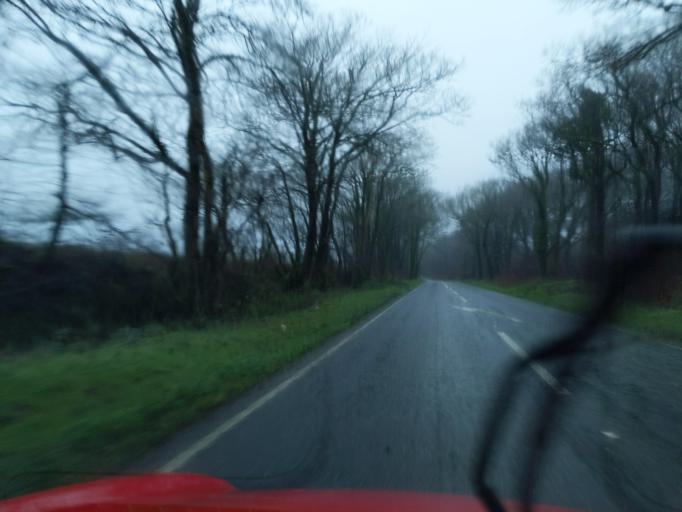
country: GB
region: England
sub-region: Cornwall
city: South Hill
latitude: 50.5268
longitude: -4.3241
